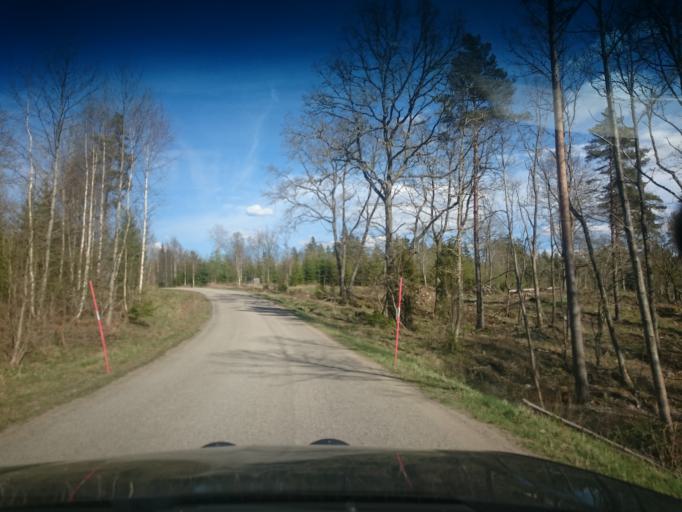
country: SE
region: Kalmar
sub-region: Hultsfreds Kommun
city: Virserum
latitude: 57.3556
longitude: 15.4904
